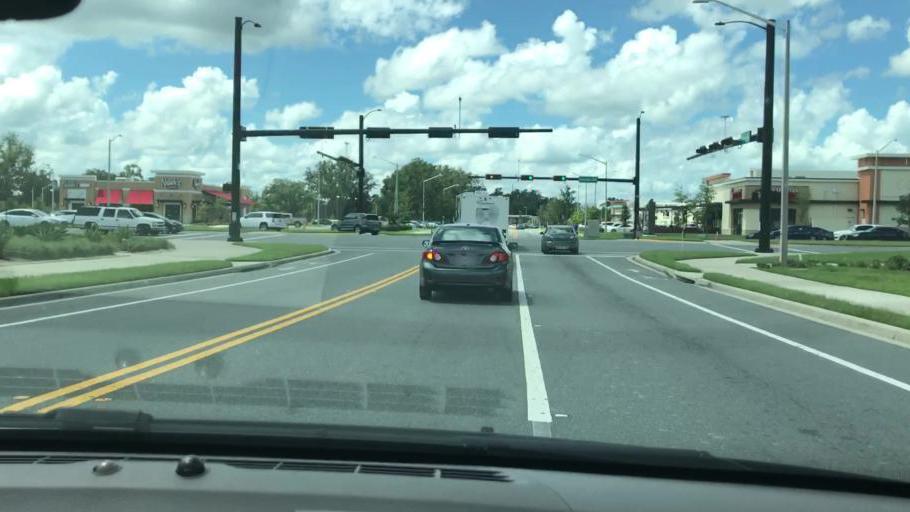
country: US
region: Florida
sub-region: Alachua County
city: Gainesville
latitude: 29.6273
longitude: -82.3841
